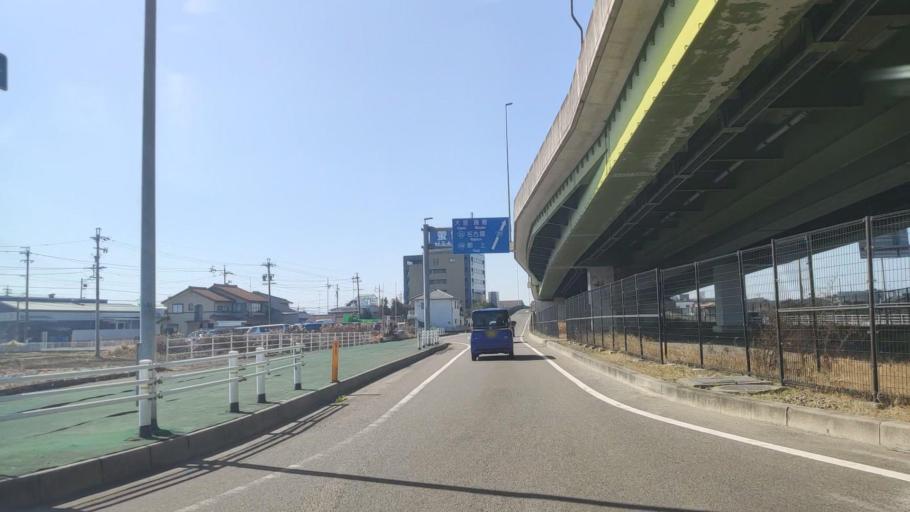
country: JP
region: Gifu
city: Kasamatsucho
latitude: 35.3886
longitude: 136.7963
